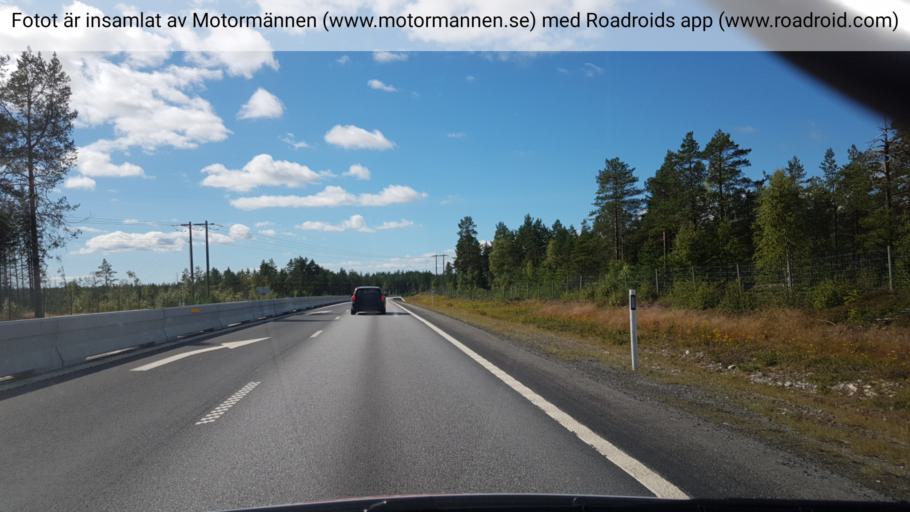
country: SE
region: Vaesterbotten
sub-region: Umea Kommun
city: Hoernefors
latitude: 63.6516
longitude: 19.9490
